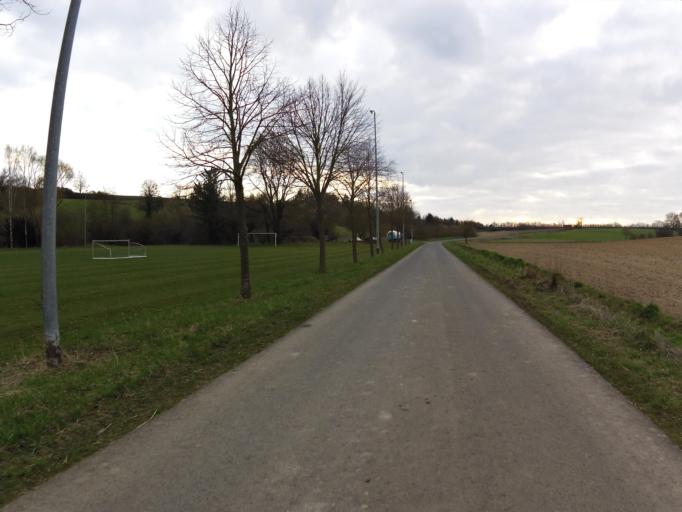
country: DE
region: Bavaria
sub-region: Regierungsbezirk Unterfranken
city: Buchbrunn
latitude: 49.7485
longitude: 10.1175
